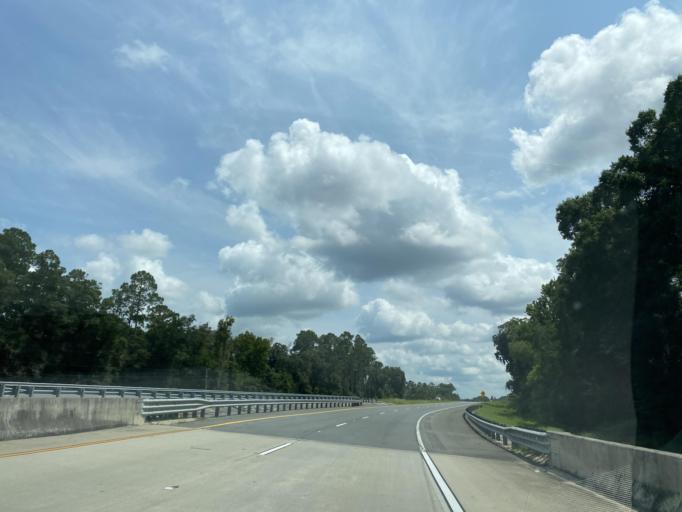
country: US
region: Georgia
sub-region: Ware County
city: Deenwood
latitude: 31.3189
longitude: -82.4572
